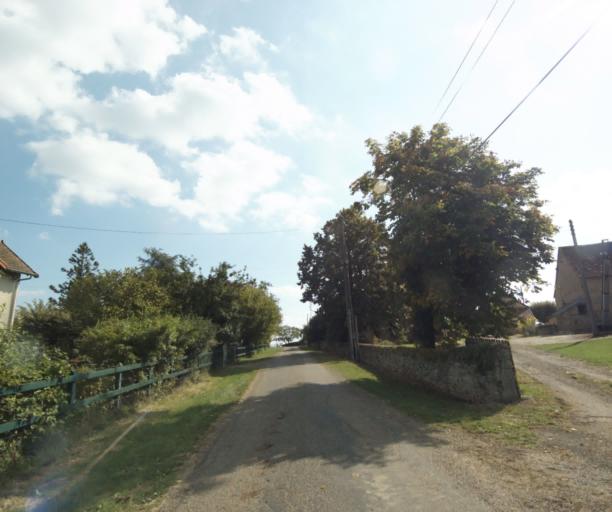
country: FR
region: Bourgogne
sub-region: Departement de Saone-et-Loire
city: Charolles
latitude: 46.4634
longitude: 4.2263
